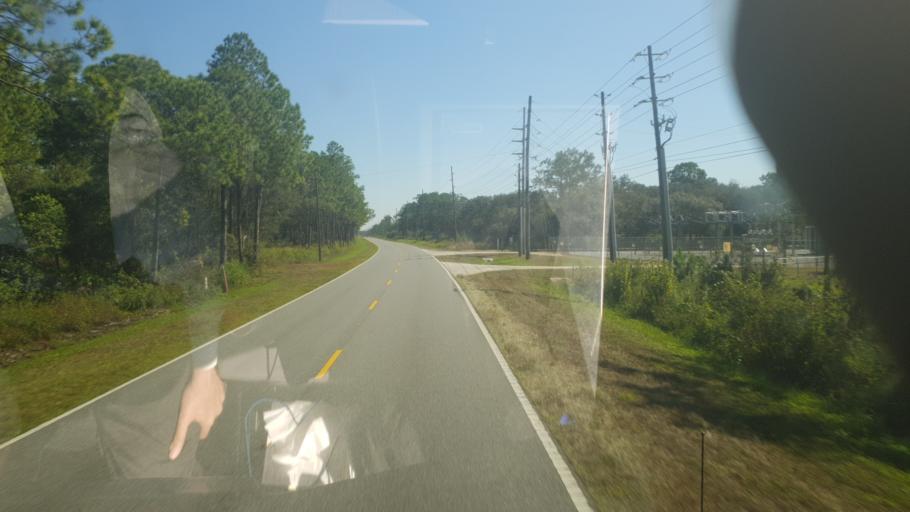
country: US
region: Florida
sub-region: Lake County
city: Four Corners
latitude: 28.3726
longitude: -81.7444
